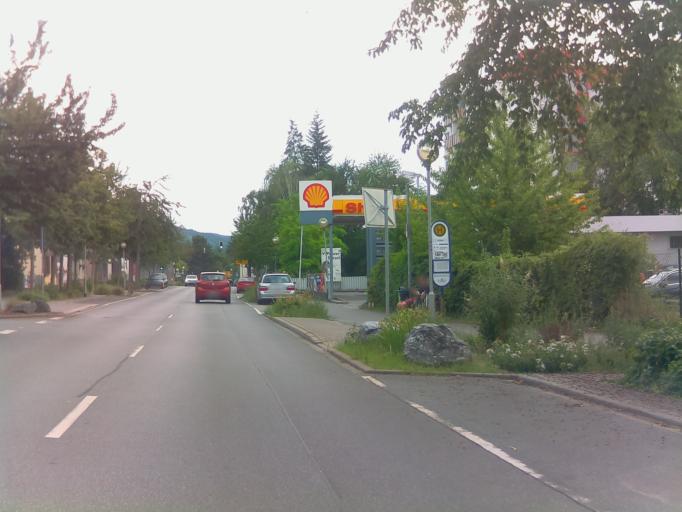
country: DE
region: Hesse
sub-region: Regierungsbezirk Darmstadt
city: Seeheim-Jugenheim
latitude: 49.7704
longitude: 8.6456
